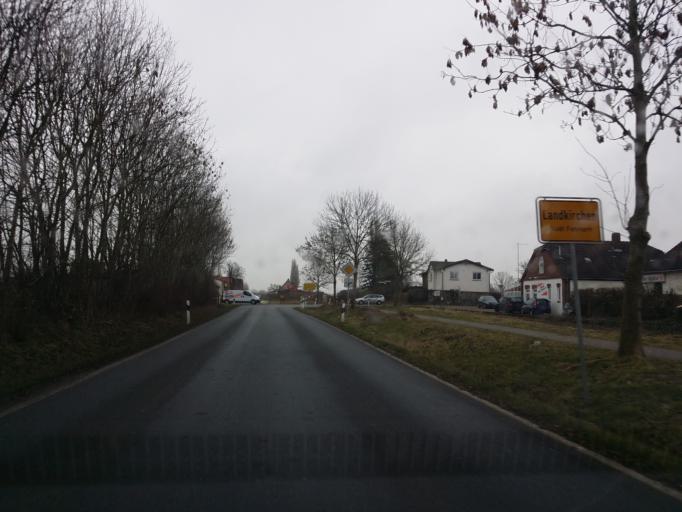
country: DE
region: Schleswig-Holstein
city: Fehmarn
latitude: 54.4537
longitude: 11.1450
